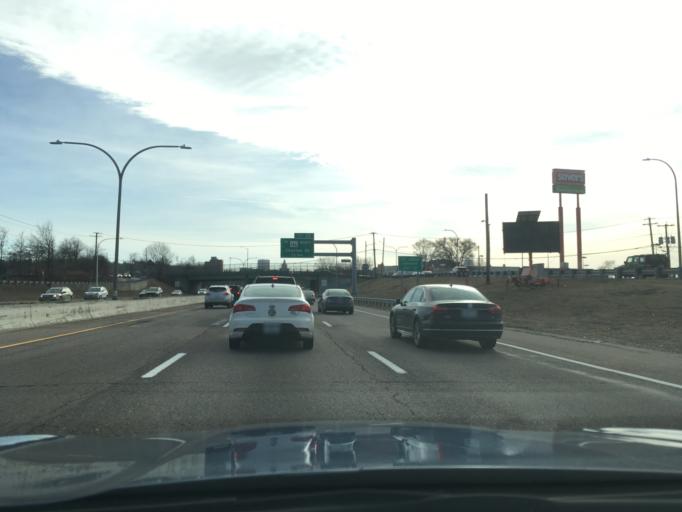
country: US
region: Rhode Island
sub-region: Providence County
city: Providence
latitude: 41.8471
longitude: -71.4113
